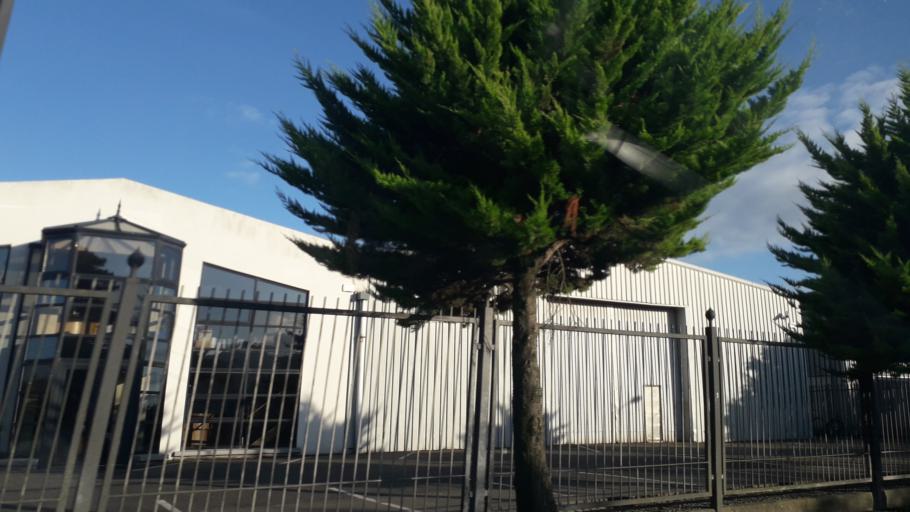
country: IE
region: Leinster
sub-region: Lu
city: Carlingford
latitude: 54.0272
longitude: -6.1354
